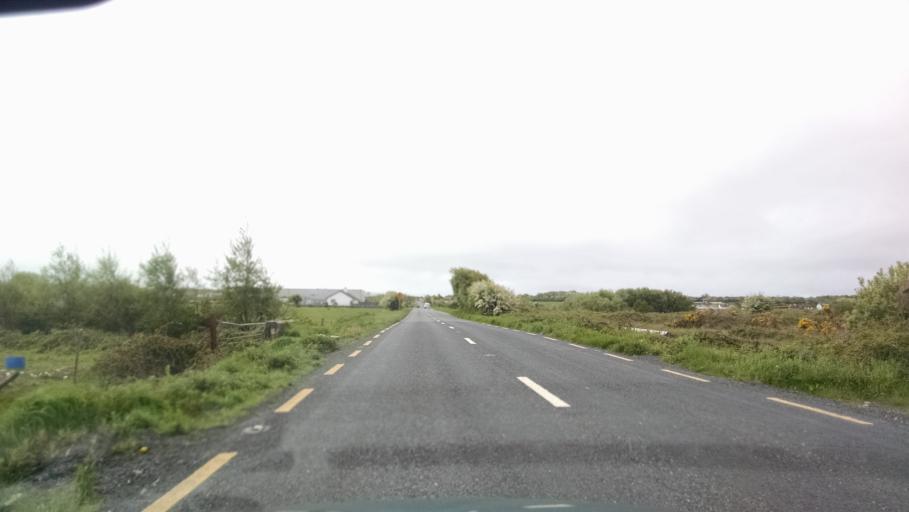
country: IE
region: Connaught
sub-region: County Galway
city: Gaillimh
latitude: 53.3227
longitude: -9.0215
